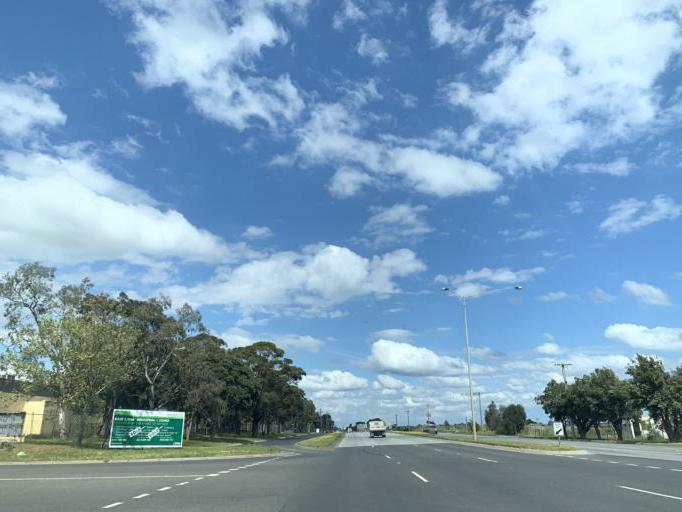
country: AU
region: Victoria
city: Heatherton
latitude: -37.9800
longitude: 145.1106
